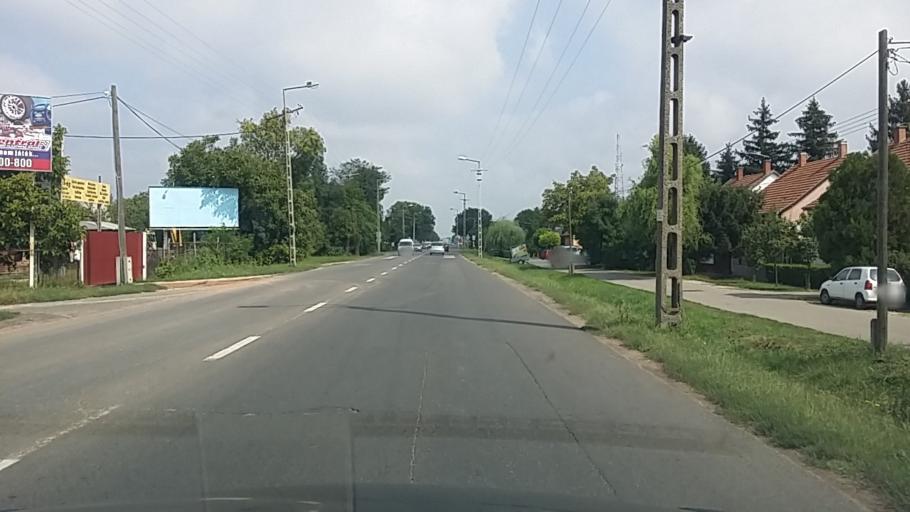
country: HU
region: Csongrad
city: Szeged
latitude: 46.2847
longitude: 20.1709
